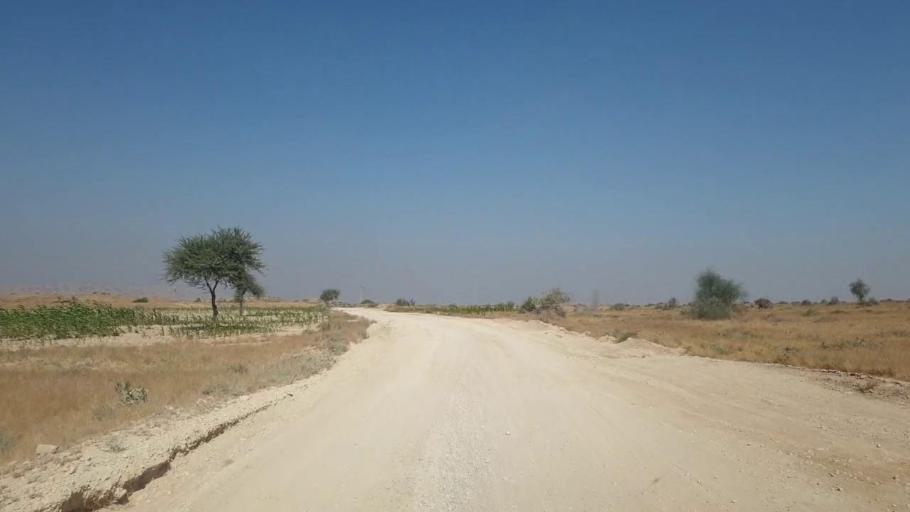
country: PK
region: Sindh
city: Thatta
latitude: 25.2351
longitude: 67.8041
